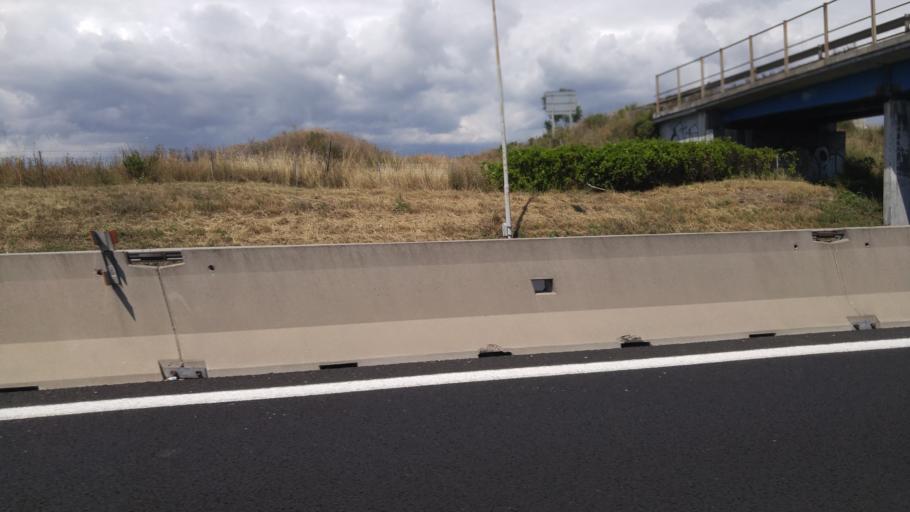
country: IT
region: Latium
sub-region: Citta metropolitana di Roma Capitale
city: Frascati
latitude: 41.8411
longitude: 12.6306
